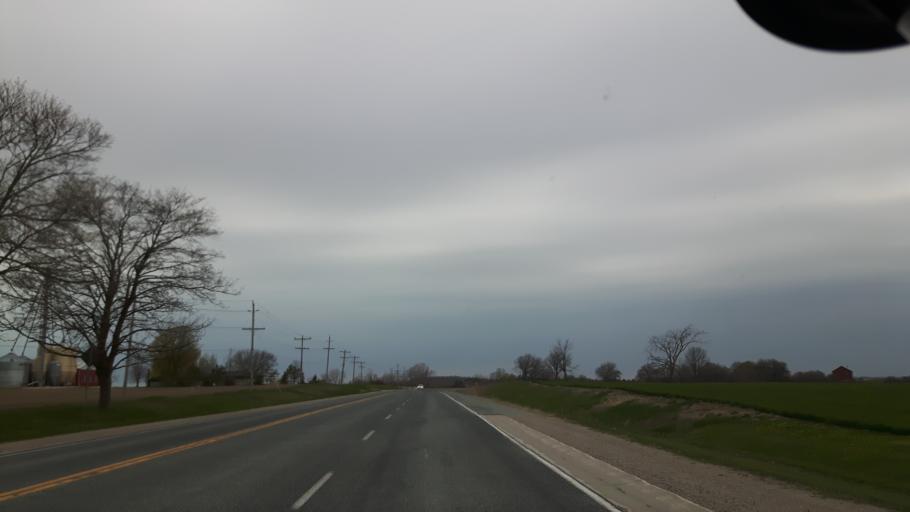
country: CA
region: Ontario
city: Goderich
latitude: 43.6528
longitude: -81.6115
